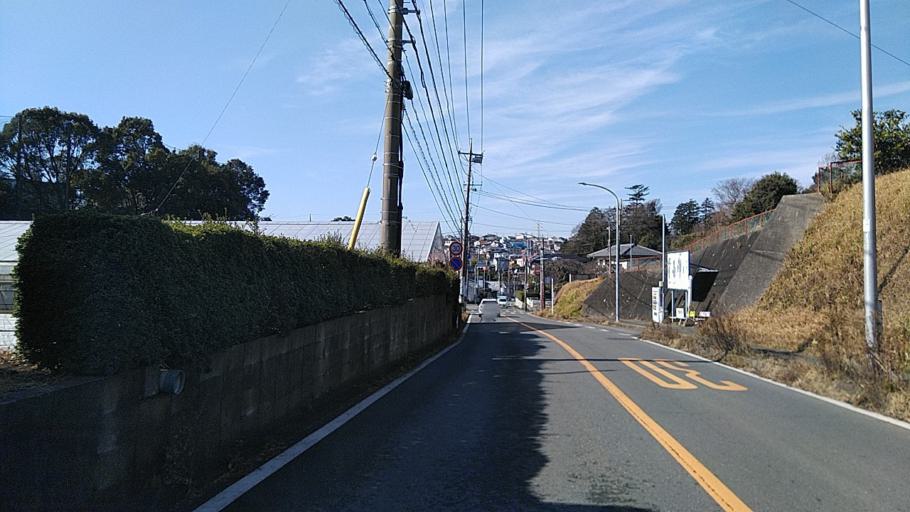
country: JP
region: Kanagawa
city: Fujisawa
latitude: 35.3925
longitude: 139.5187
